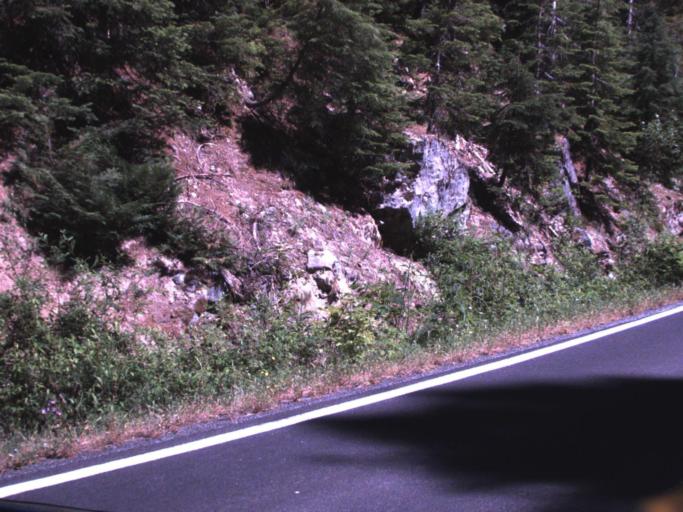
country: US
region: Washington
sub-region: King County
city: Enumclaw
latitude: 46.8307
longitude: -121.5204
